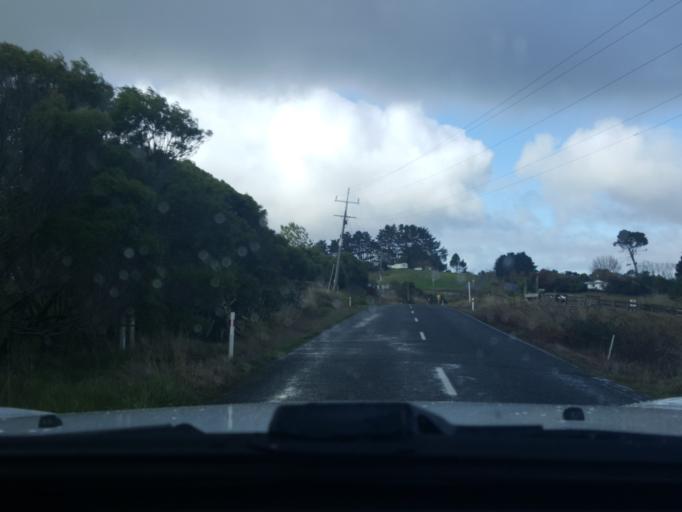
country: NZ
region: Waikato
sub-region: Waikato District
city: Te Kauwhata
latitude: -37.4415
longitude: 175.0797
